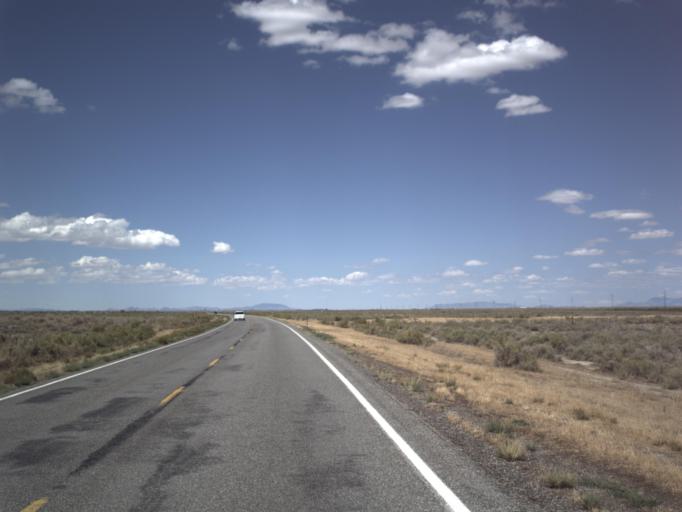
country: US
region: Utah
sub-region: Millard County
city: Delta
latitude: 39.2554
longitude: -112.4424
